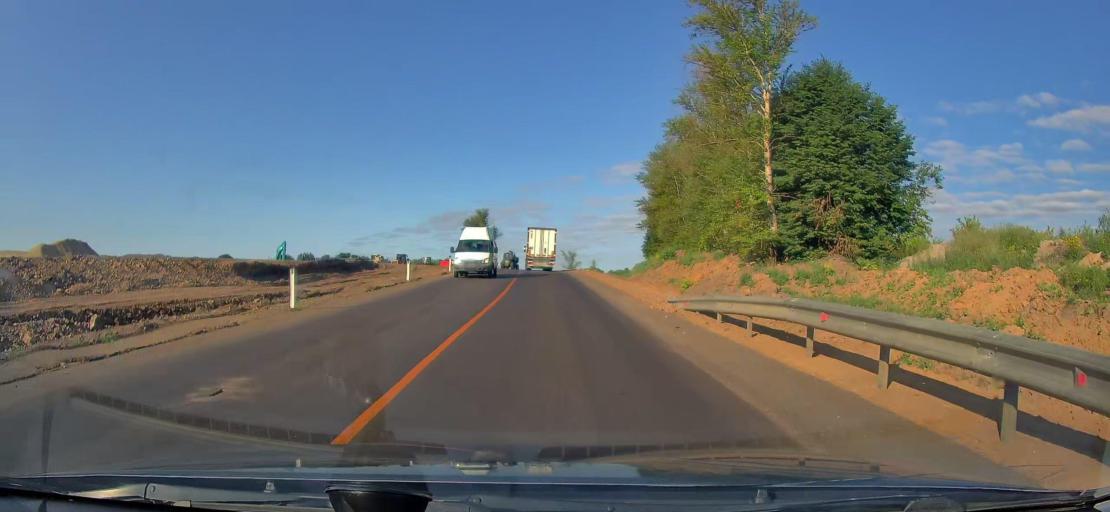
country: RU
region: Tula
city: Bol'shoye Skuratovo
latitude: 53.4436
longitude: 36.8334
